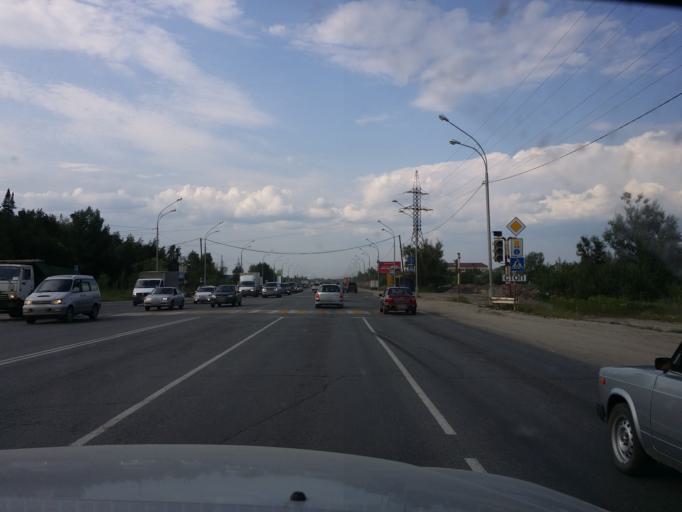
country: RU
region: Khanty-Mansiyskiy Avtonomnyy Okrug
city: Nizhnevartovsk
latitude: 60.9549
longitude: 76.5302
